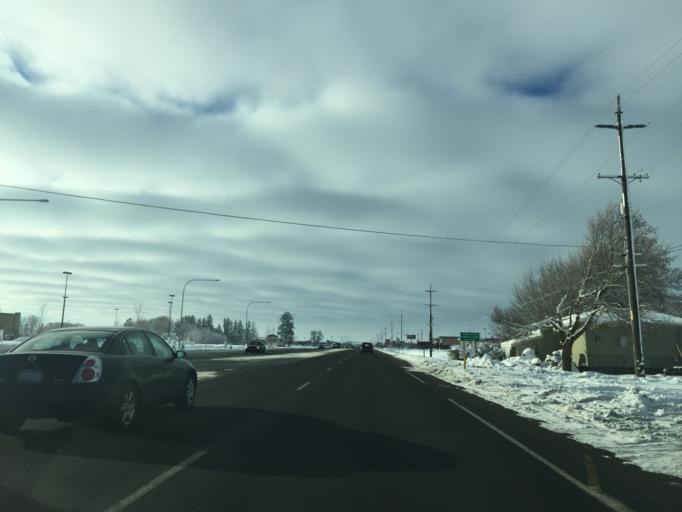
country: US
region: Washington
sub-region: Spokane County
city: Airway Heights
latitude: 47.6432
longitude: -117.5499
